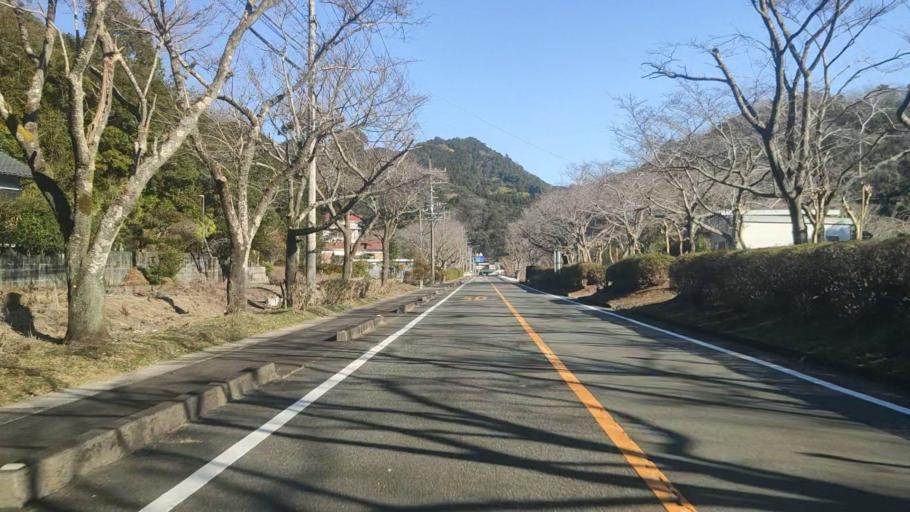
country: JP
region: Miyazaki
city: Nobeoka
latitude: 32.6424
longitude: 131.7449
